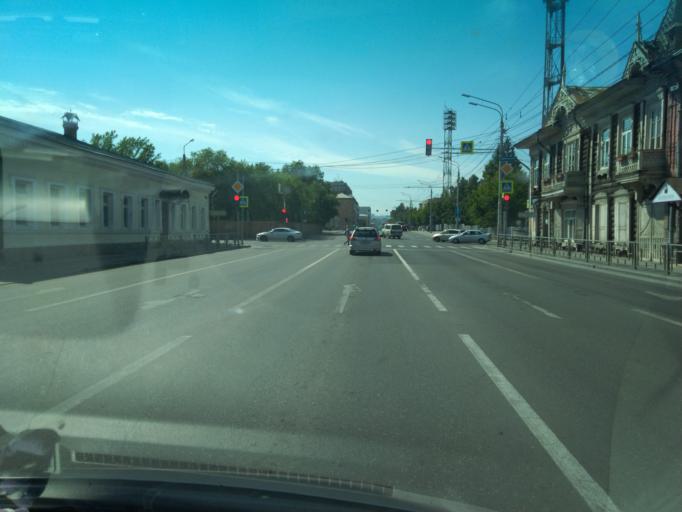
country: RU
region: Krasnoyarskiy
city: Krasnoyarsk
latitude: 56.0133
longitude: 92.8674
